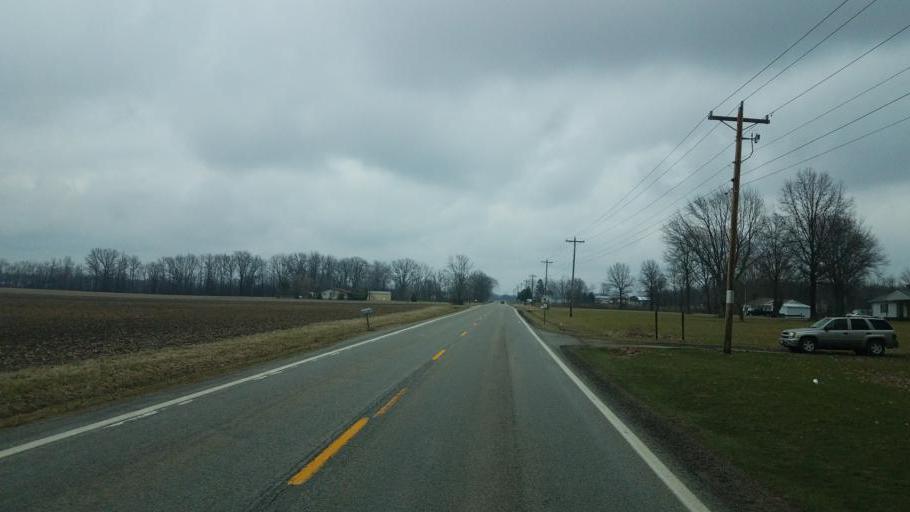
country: US
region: Ohio
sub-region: Delaware County
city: Ashley
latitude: 40.4065
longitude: -82.8881
